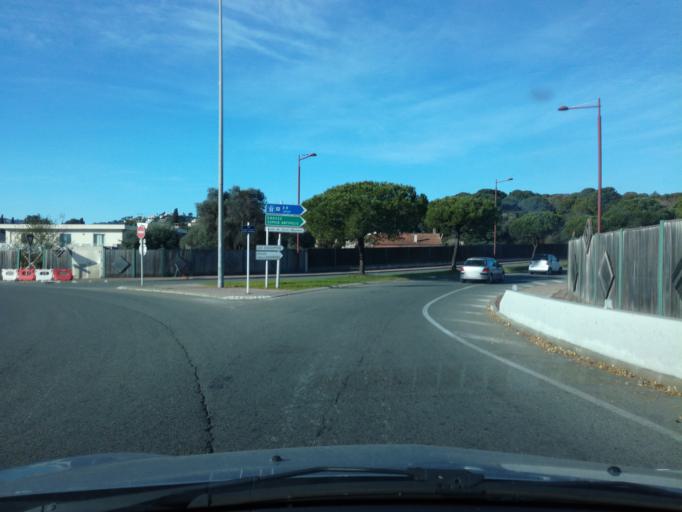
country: FR
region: Provence-Alpes-Cote d'Azur
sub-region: Departement des Alpes-Maritimes
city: Vallauris
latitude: 43.5790
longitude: 7.0906
